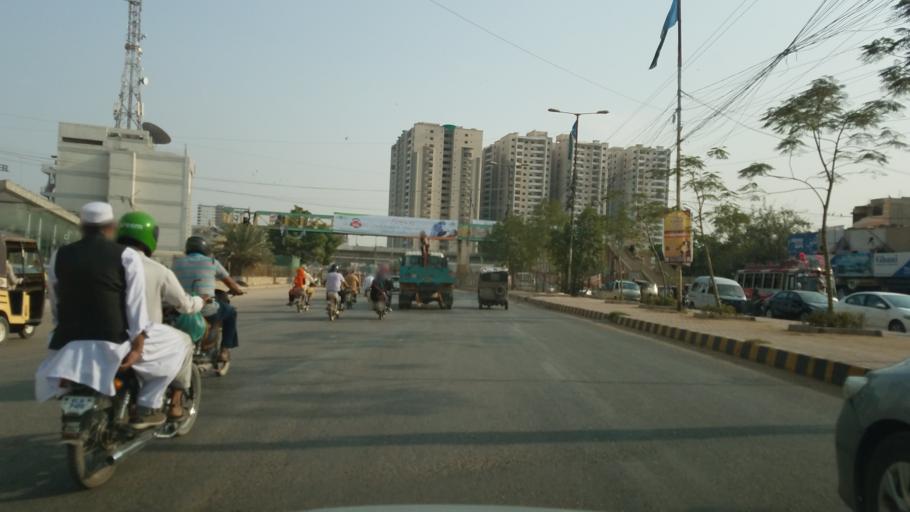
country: PK
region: Sindh
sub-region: Karachi District
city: Karachi
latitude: 24.9309
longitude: 67.0864
